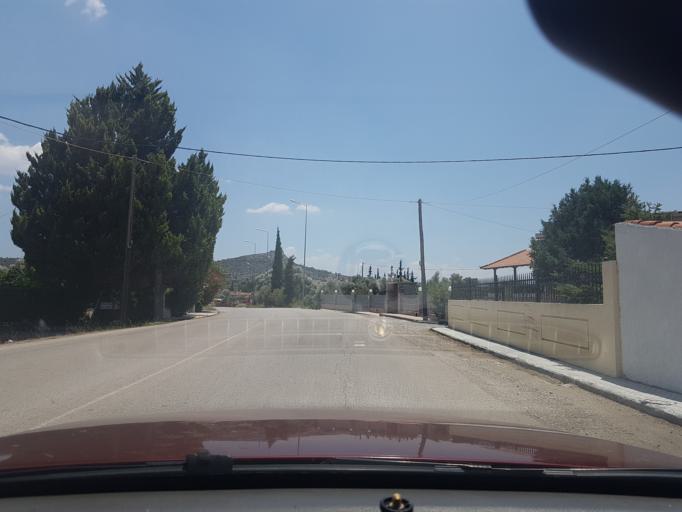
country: GR
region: Central Greece
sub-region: Nomos Evvoias
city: Afration
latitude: 38.4538
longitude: 23.6776
